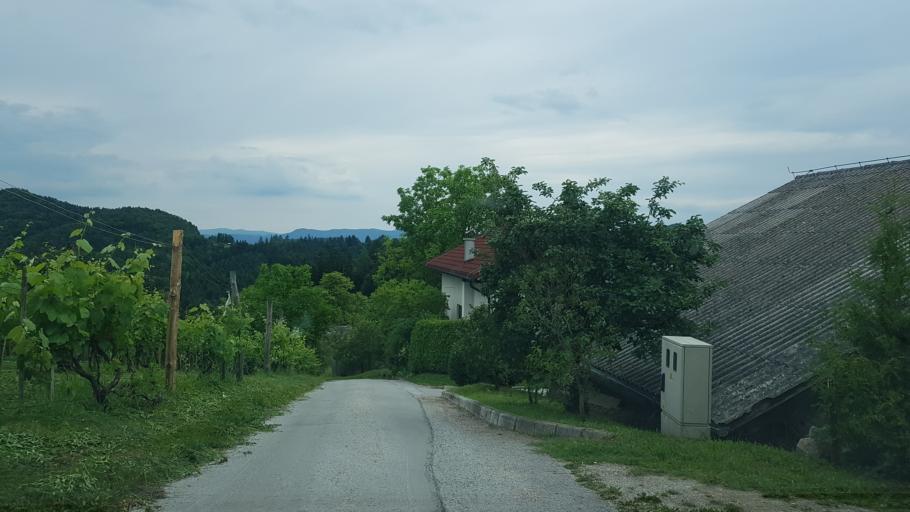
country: SI
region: Dobrna
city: Dobrna
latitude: 46.3449
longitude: 15.2559
